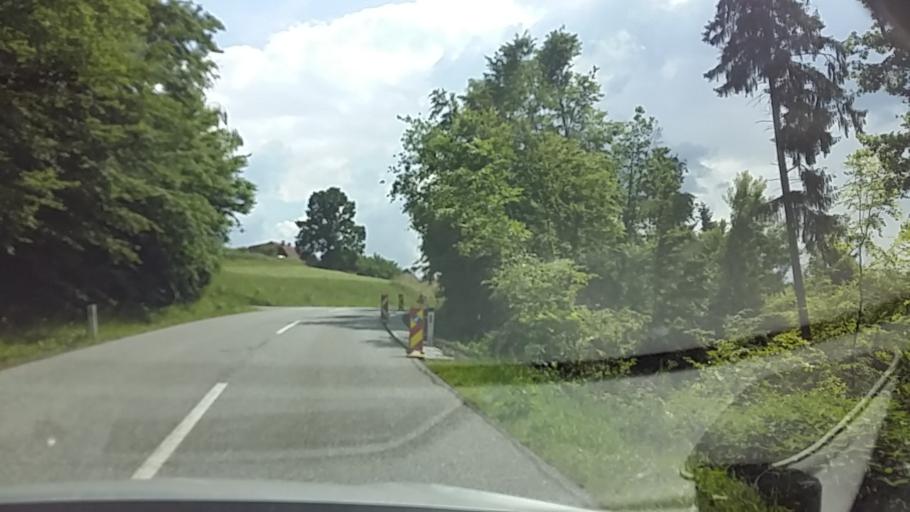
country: AT
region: Styria
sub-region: Politischer Bezirk Suedoststeiermark
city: Breitenfeld an der Rittschein
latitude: 47.0251
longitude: 15.9506
